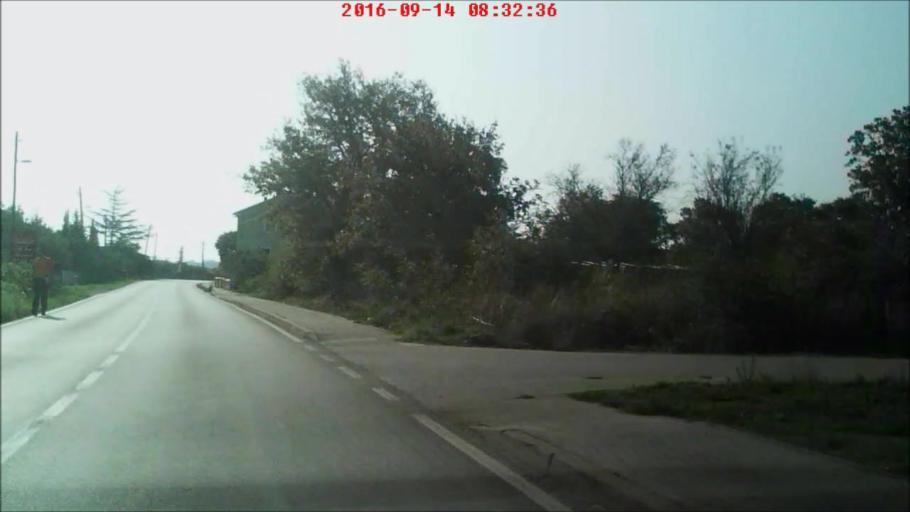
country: HR
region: Zadarska
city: Policnik
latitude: 44.1619
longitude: 15.3069
